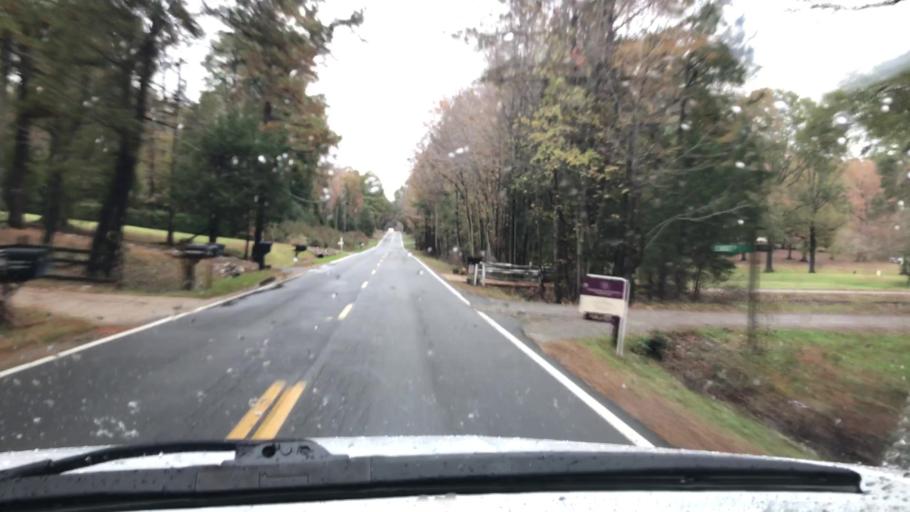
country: US
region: Virginia
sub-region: Henrico County
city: Short Pump
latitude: 37.6254
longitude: -77.6896
